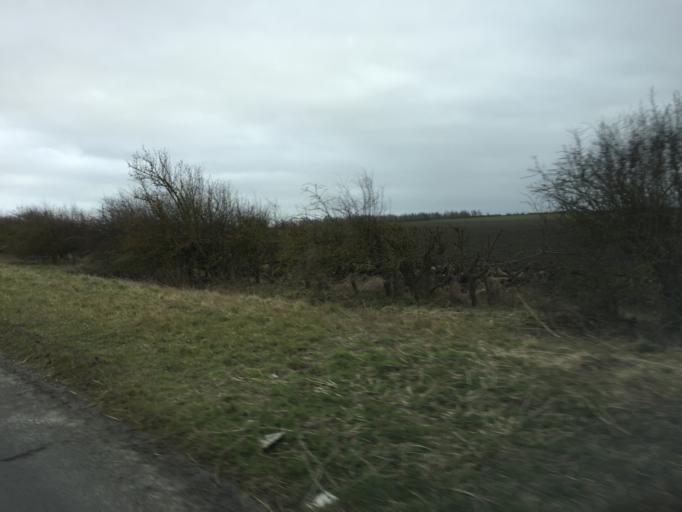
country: GB
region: England
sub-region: Oxfordshire
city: Harwell
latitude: 51.5935
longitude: -1.2847
